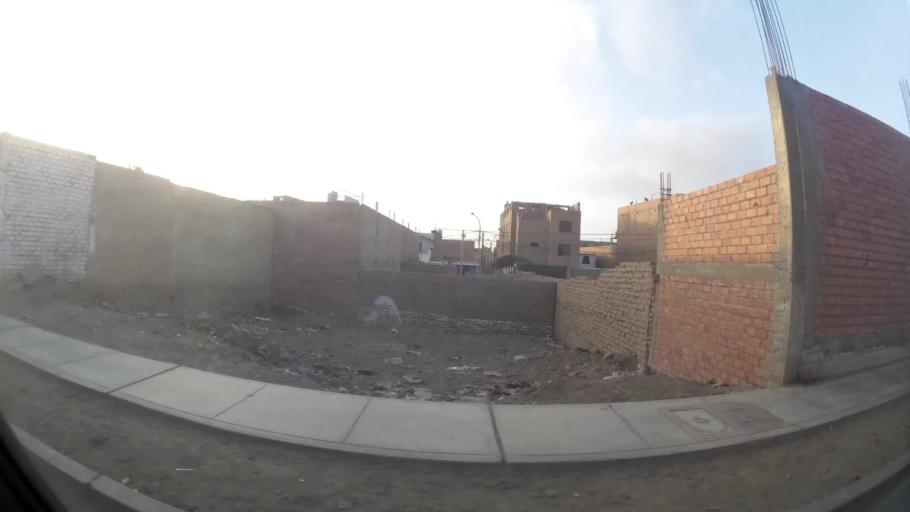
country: PE
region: Lima
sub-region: Huaura
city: Huacho
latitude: -11.1099
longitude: -77.6008
